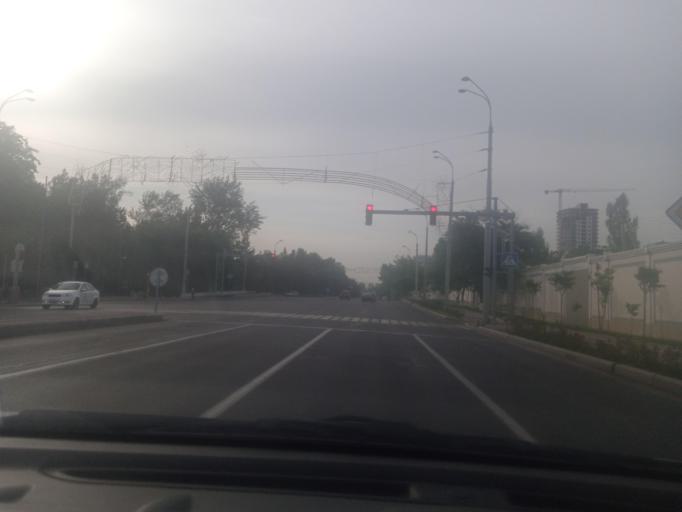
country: UZ
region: Toshkent
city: Salor
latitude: 41.3269
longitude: 69.3581
